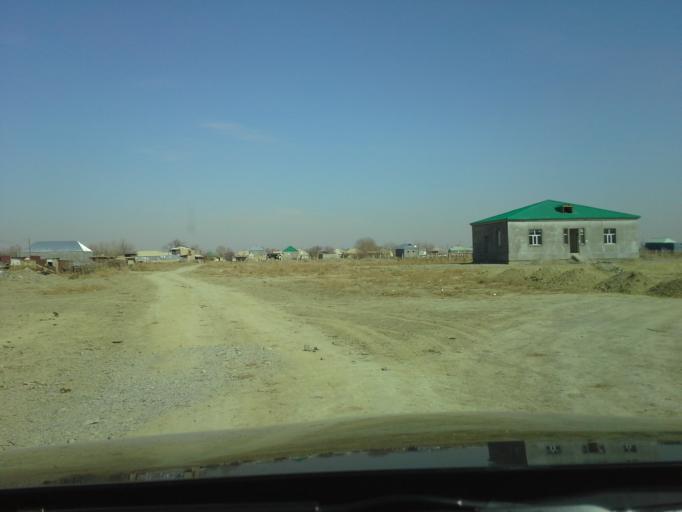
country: TM
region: Ahal
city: Abadan
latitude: 38.1016
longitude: 58.0329
